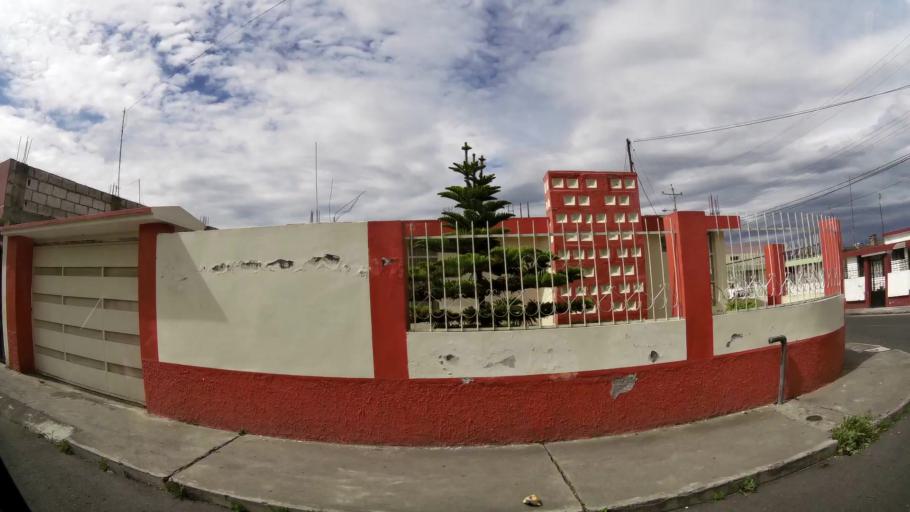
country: EC
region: Cotopaxi
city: Latacunga
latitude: -0.9273
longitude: -78.6091
